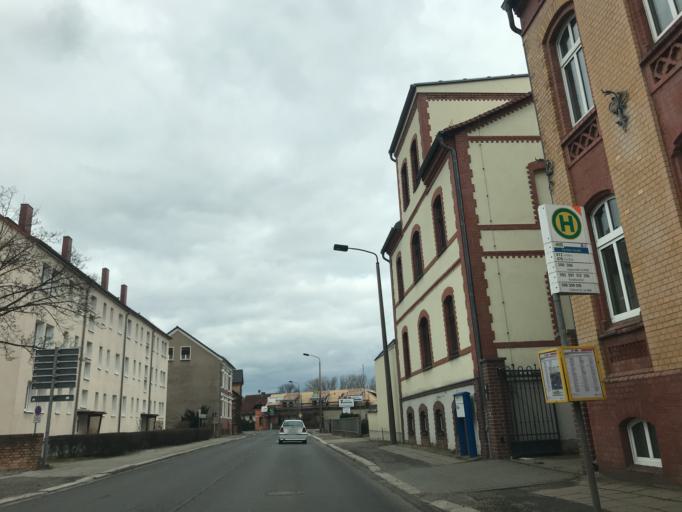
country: DE
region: Brandenburg
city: Luebben
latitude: 51.9428
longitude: 13.8927
